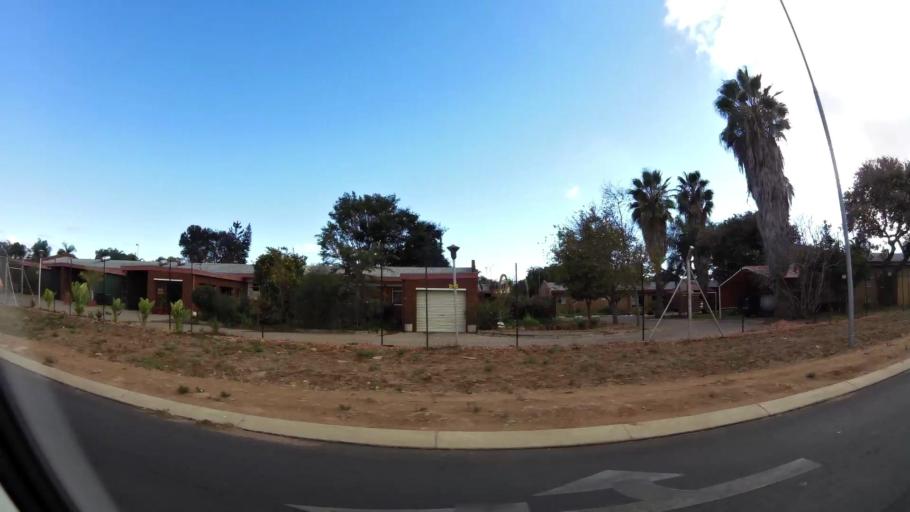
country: ZA
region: Limpopo
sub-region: Capricorn District Municipality
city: Polokwane
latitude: -23.9174
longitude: 29.4695
